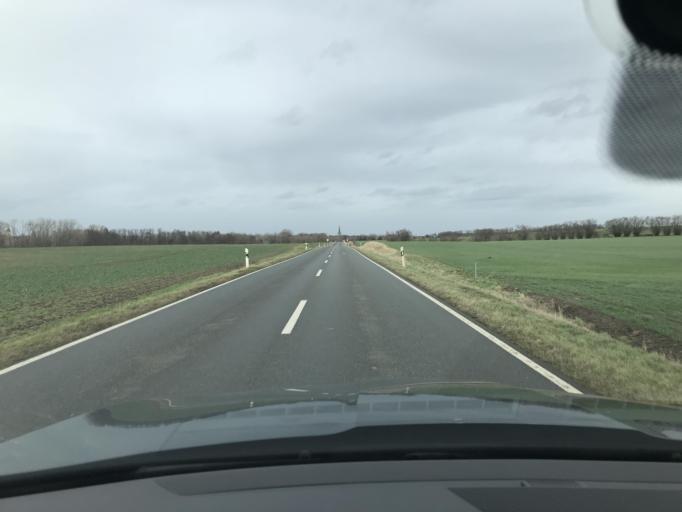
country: DE
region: Saxony-Anhalt
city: Groeningen
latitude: 51.9237
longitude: 11.1986
